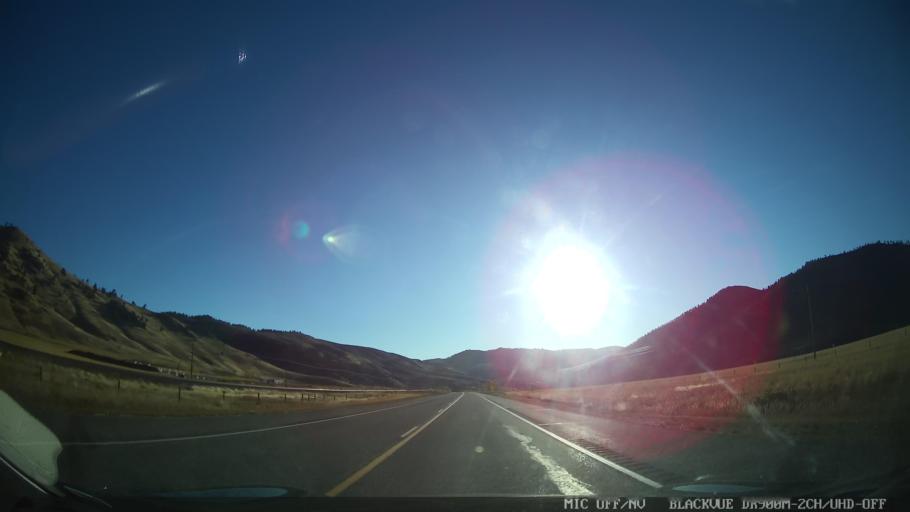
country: US
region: Colorado
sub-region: Grand County
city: Hot Sulphur Springs
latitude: 40.0508
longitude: -106.1448
